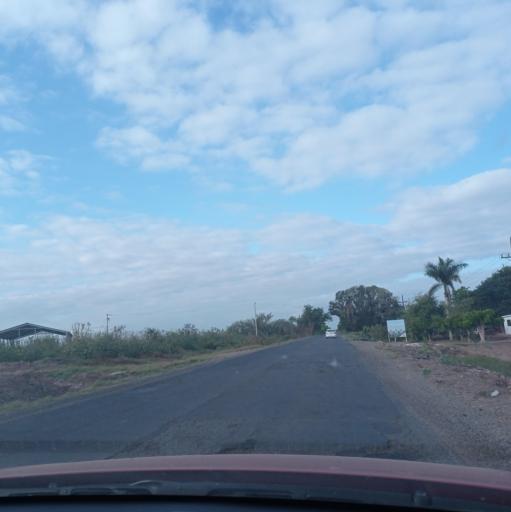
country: MX
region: Sinaloa
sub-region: Guasave
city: Las Quemazones
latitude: 25.6567
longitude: -108.5242
